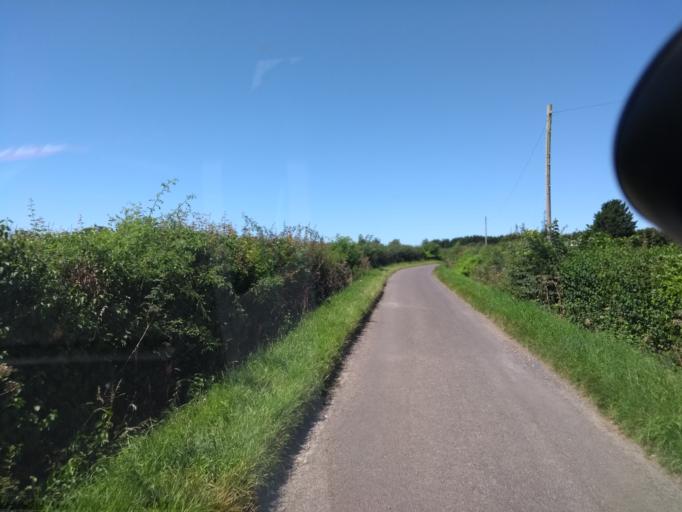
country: GB
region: England
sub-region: Somerset
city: Curry Rivel
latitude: 51.0284
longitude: -2.8718
